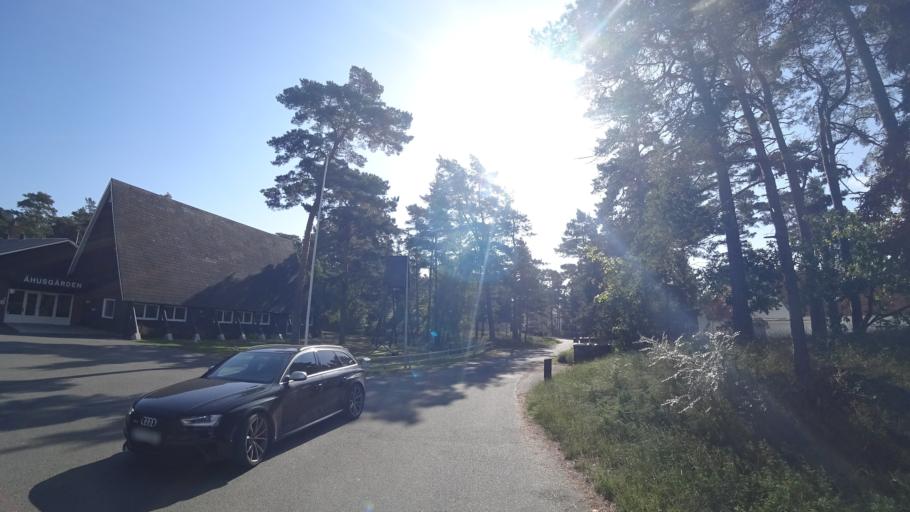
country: SE
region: Skane
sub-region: Kristianstads Kommun
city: Ahus
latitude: 55.9211
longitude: 14.3016
